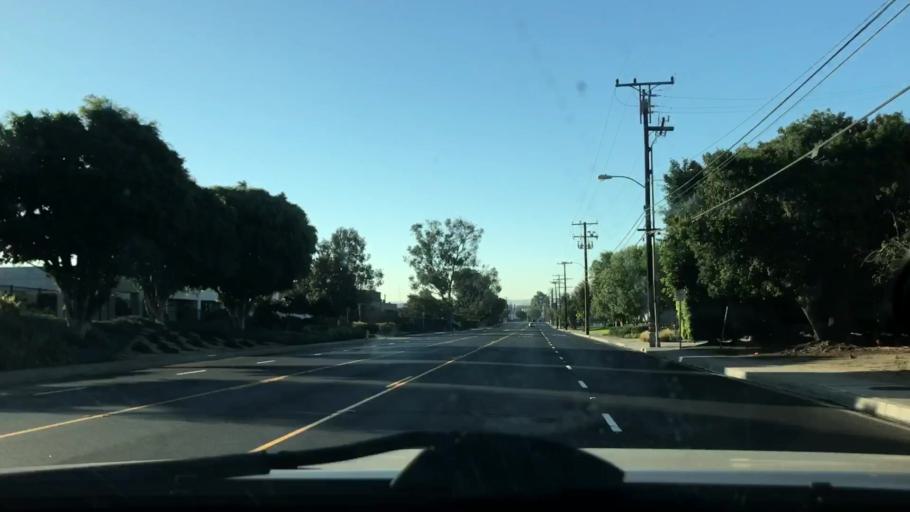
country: US
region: California
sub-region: Los Angeles County
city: Del Aire
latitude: 33.9145
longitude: -118.3832
